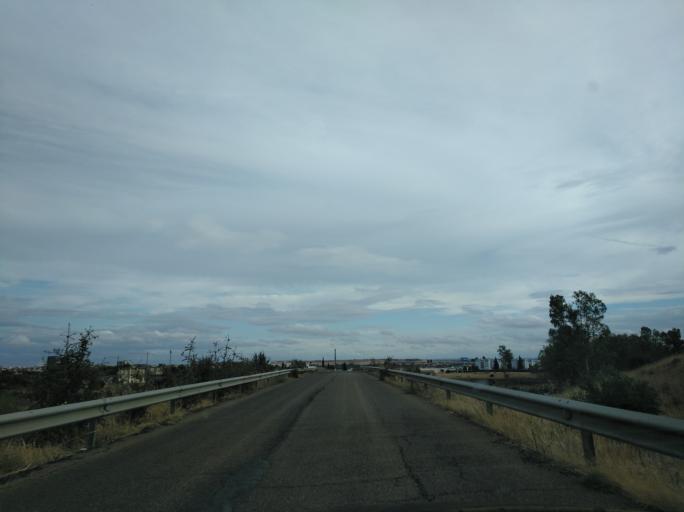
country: ES
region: Extremadura
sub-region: Provincia de Badajoz
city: Badajoz
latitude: 38.8897
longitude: -7.0163
